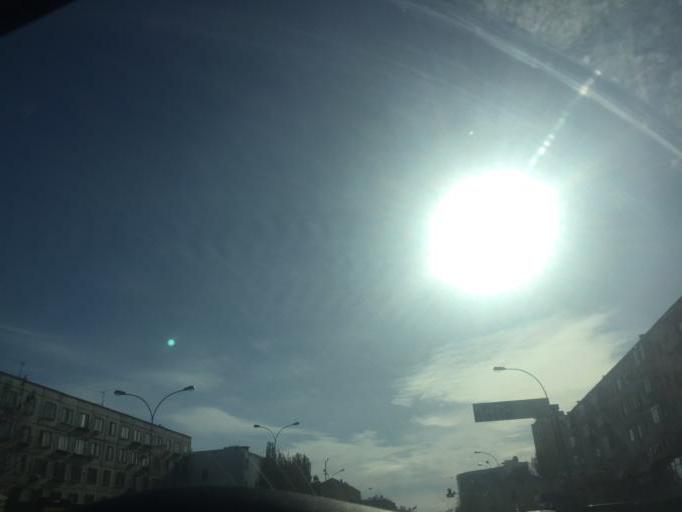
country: KZ
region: Astana Qalasy
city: Astana
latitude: 51.1710
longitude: 71.4123
